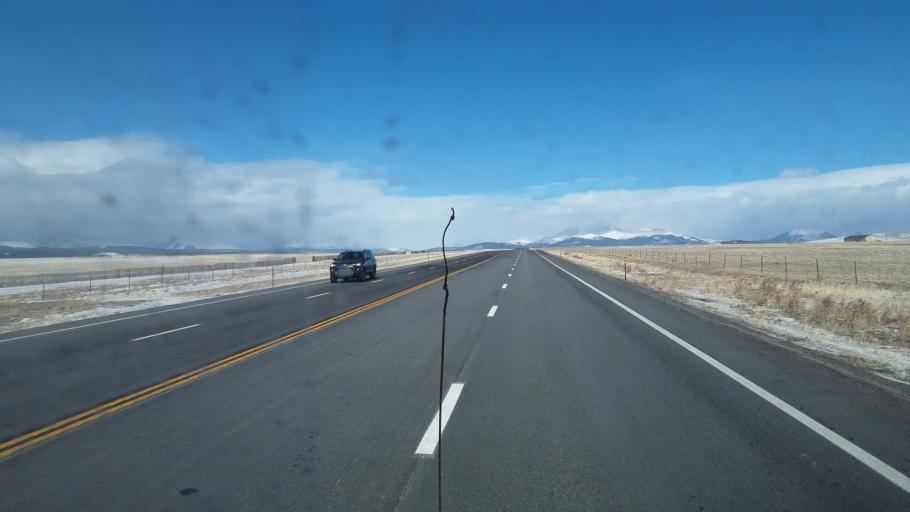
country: US
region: Colorado
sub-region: Park County
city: Fairplay
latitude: 39.1357
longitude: -105.9958
